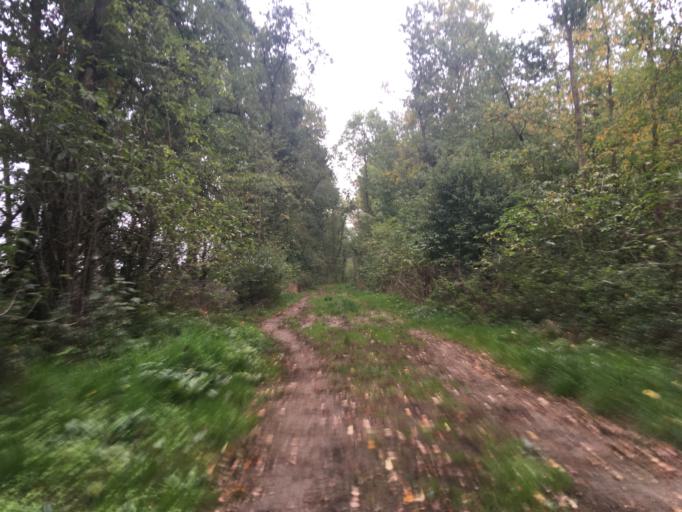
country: DE
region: Brandenburg
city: Falkensee
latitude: 52.5271
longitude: 13.0884
